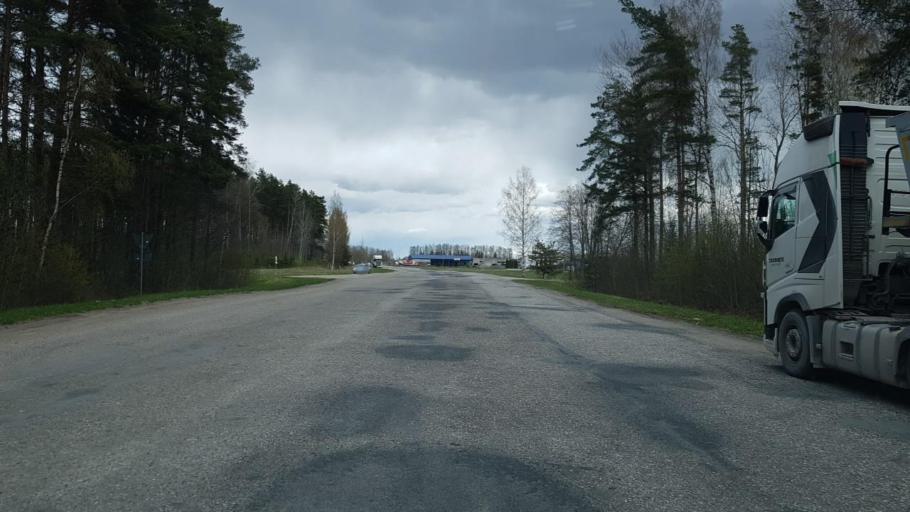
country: EE
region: Tartu
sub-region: Tartu linn
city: Tartu
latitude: 58.3879
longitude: 26.6716
